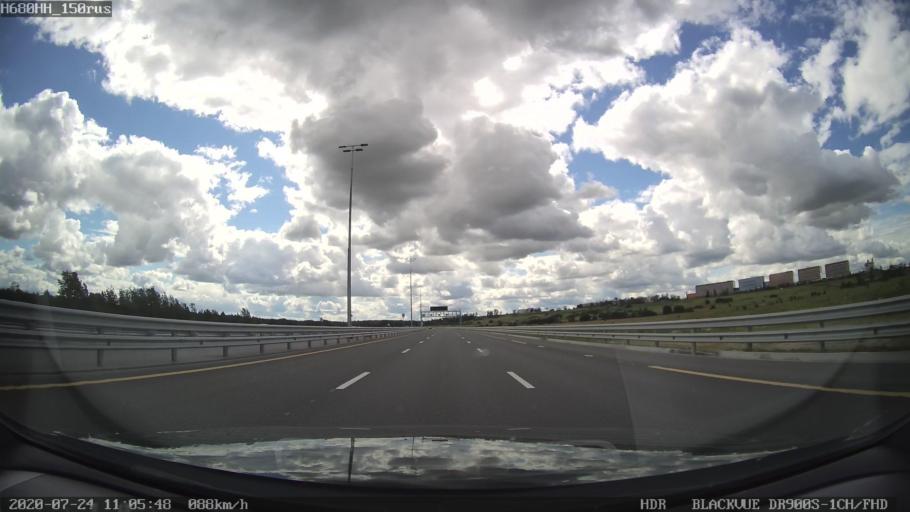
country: RU
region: St.-Petersburg
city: Shushary
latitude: 59.7723
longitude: 30.3623
